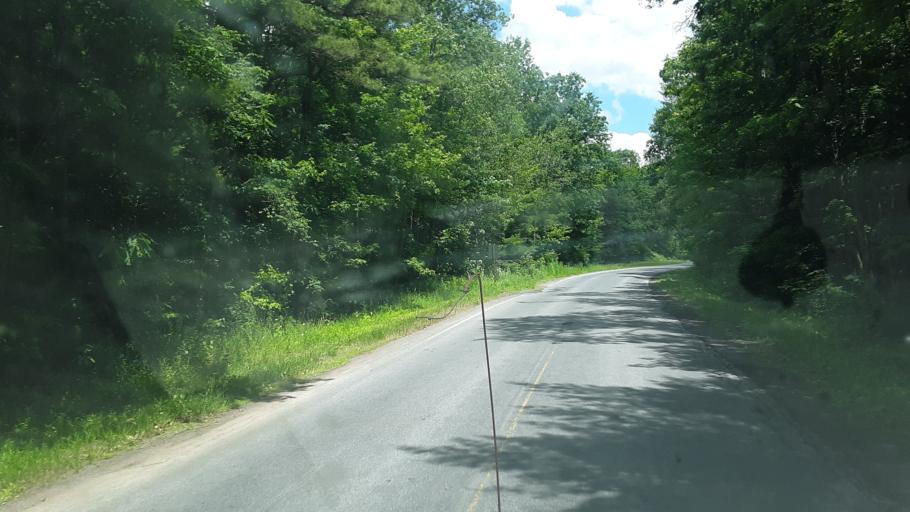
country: US
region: New York
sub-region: Oneida County
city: Rome
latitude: 43.2630
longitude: -75.5837
